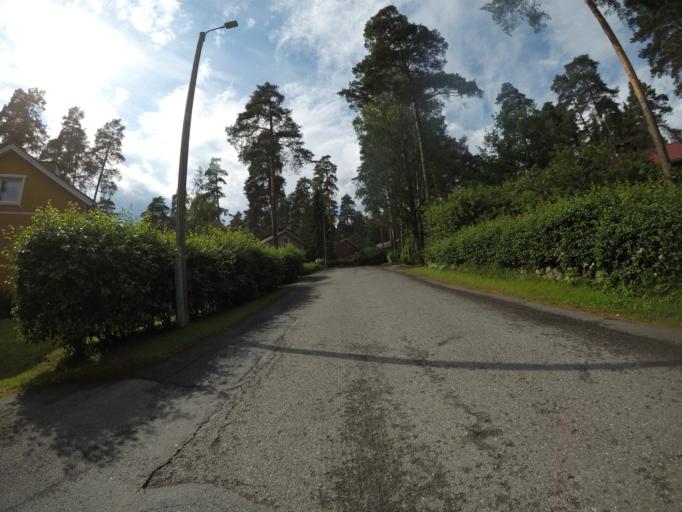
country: FI
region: Haeme
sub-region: Haemeenlinna
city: Haemeenlinna
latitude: 61.0135
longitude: 24.4664
